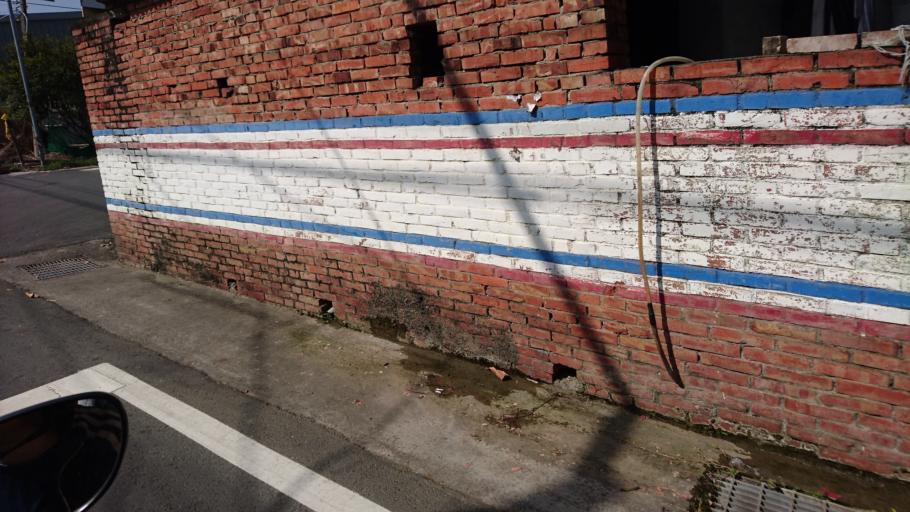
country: TW
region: Taiwan
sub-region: Hsinchu
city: Hsinchu
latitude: 24.7296
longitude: 120.9361
